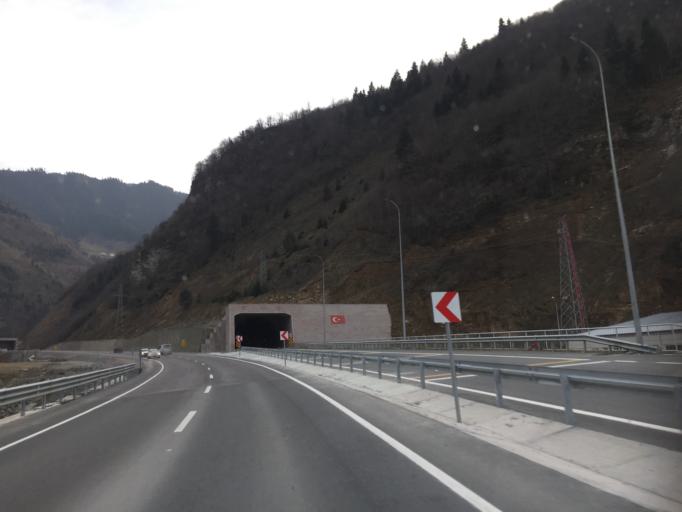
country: TR
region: Trabzon
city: Macka
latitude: 40.7582
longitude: 39.5625
